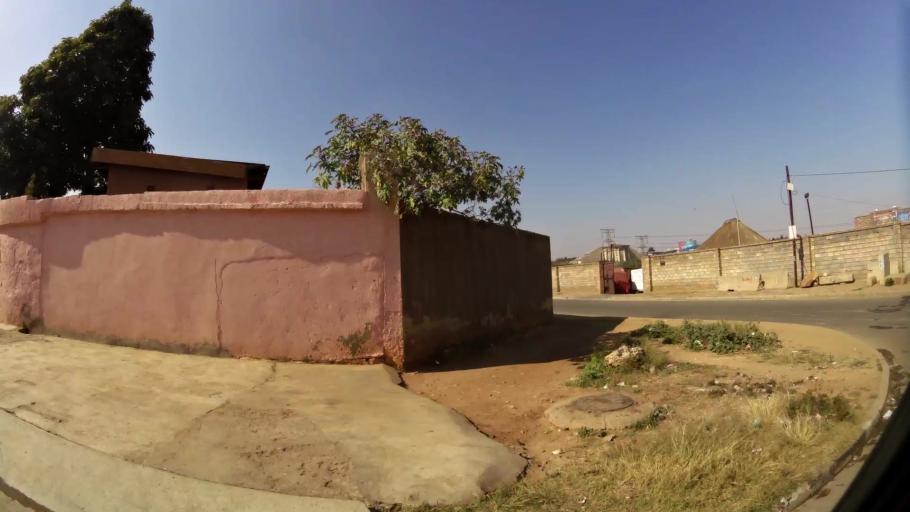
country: ZA
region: Gauteng
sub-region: City of Johannesburg Metropolitan Municipality
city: Soweto
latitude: -26.2521
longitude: 27.9385
